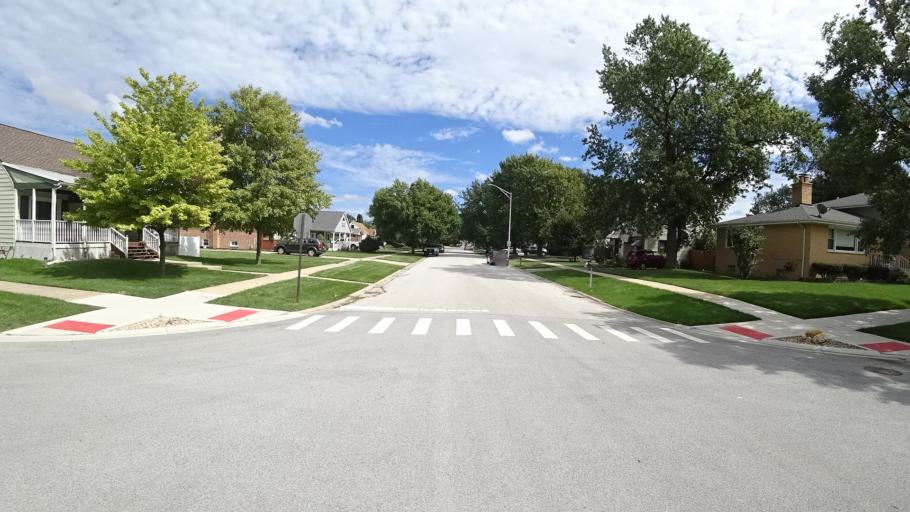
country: US
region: Illinois
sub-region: Cook County
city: Chicago Ridge
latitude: 41.7166
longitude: -87.7918
